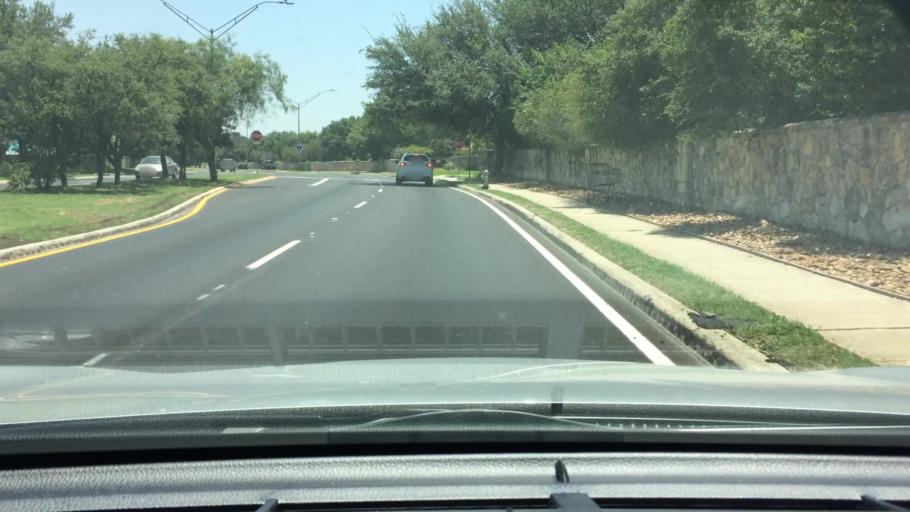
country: US
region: Texas
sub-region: Bexar County
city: Shavano Park
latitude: 29.5587
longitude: -98.5795
